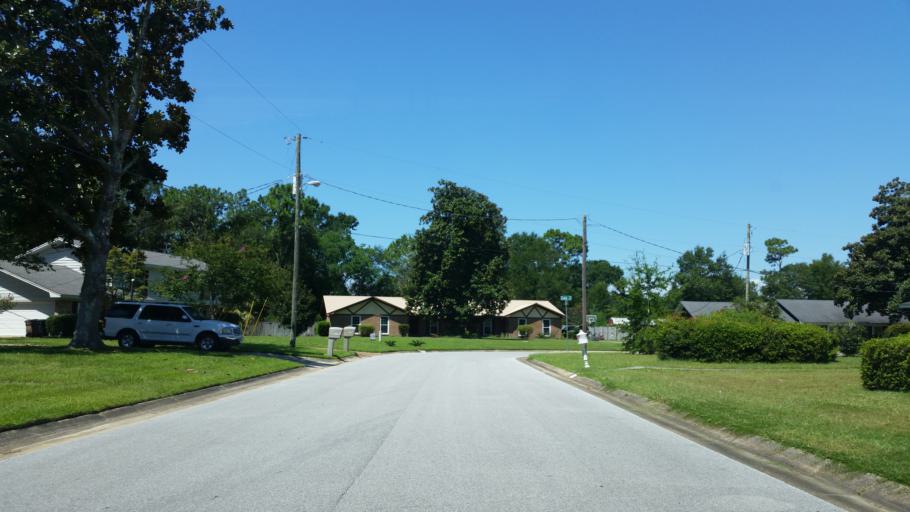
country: US
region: Florida
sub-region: Escambia County
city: Ferry Pass
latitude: 30.5064
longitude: -87.1887
